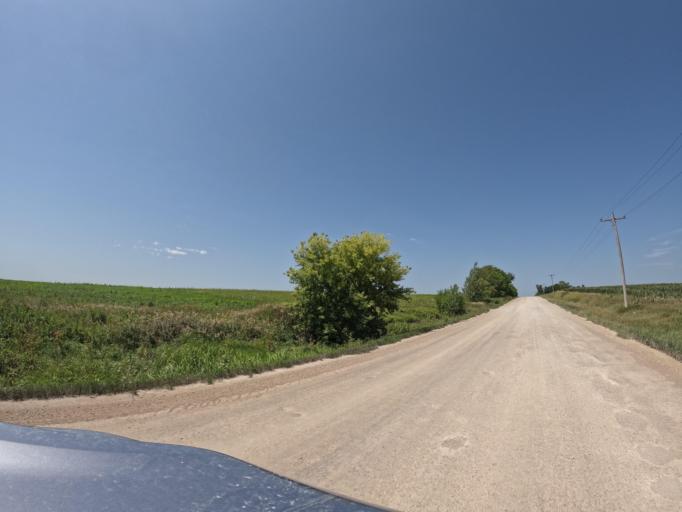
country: US
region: Iowa
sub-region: Henry County
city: Mount Pleasant
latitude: 40.9375
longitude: -91.5196
